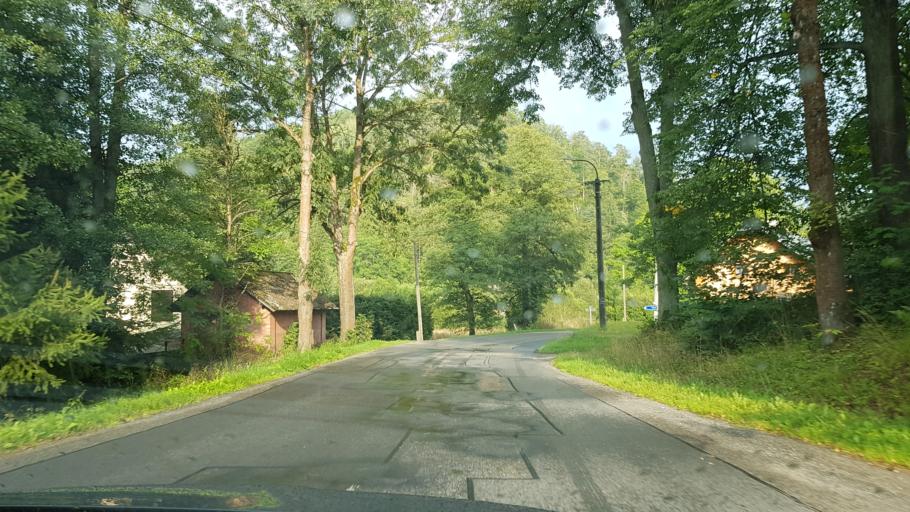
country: CZ
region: Olomoucky
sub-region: Okres Sumperk
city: Hanusovice
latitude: 50.0897
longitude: 16.8928
